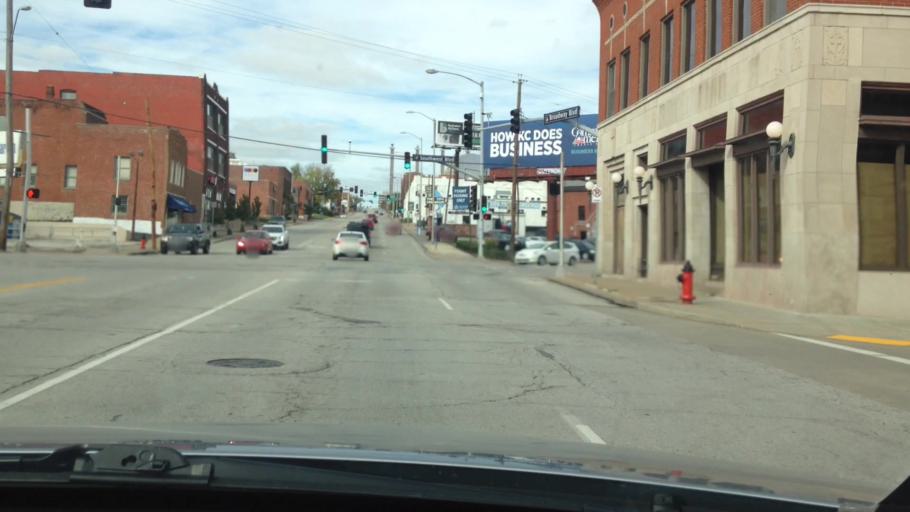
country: US
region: Missouri
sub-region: Jackson County
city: Kansas City
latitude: 39.0874
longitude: -94.5889
